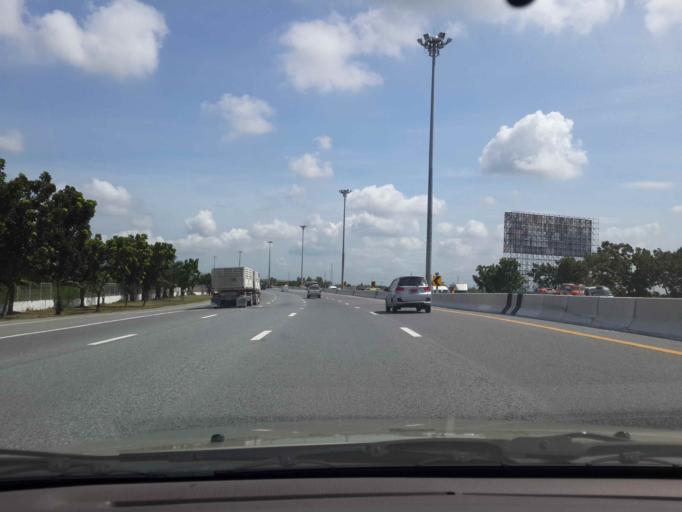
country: TH
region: Chon Buri
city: Phan Thong
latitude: 13.4938
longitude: 101.0463
